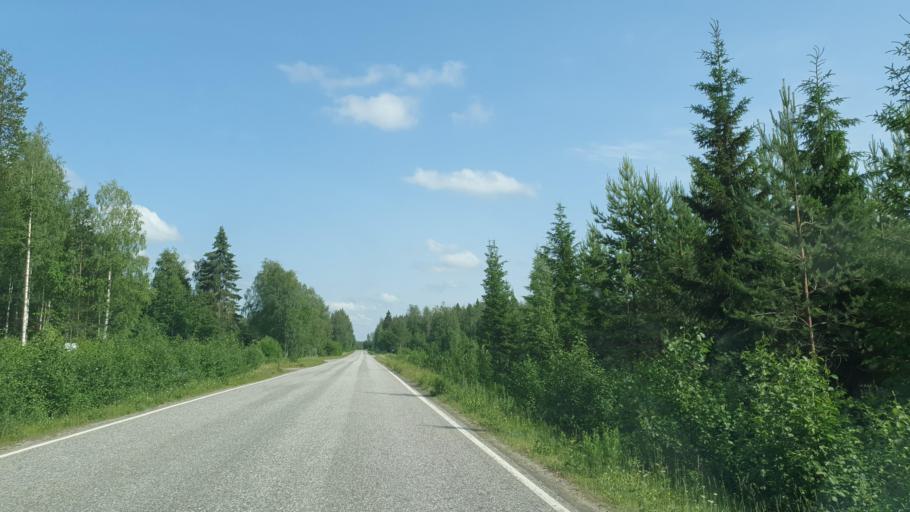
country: FI
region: Kainuu
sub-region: Kehys-Kainuu
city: Kuhmo
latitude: 64.1279
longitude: 29.5986
